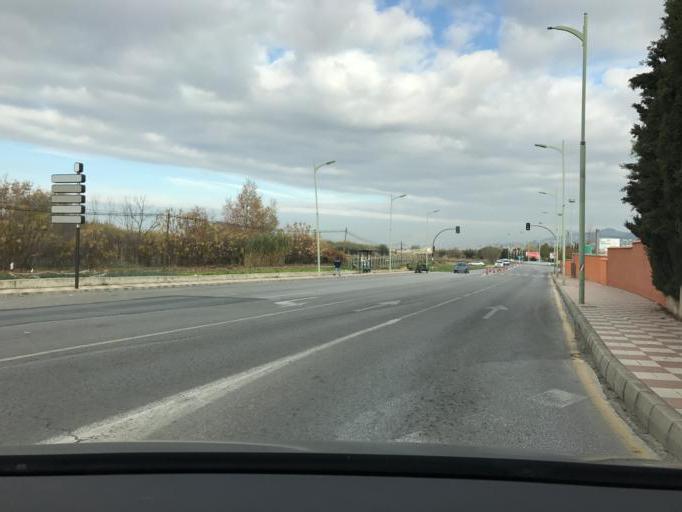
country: ES
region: Andalusia
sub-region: Provincia de Granada
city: Zubia
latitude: 37.1267
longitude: -3.5857
